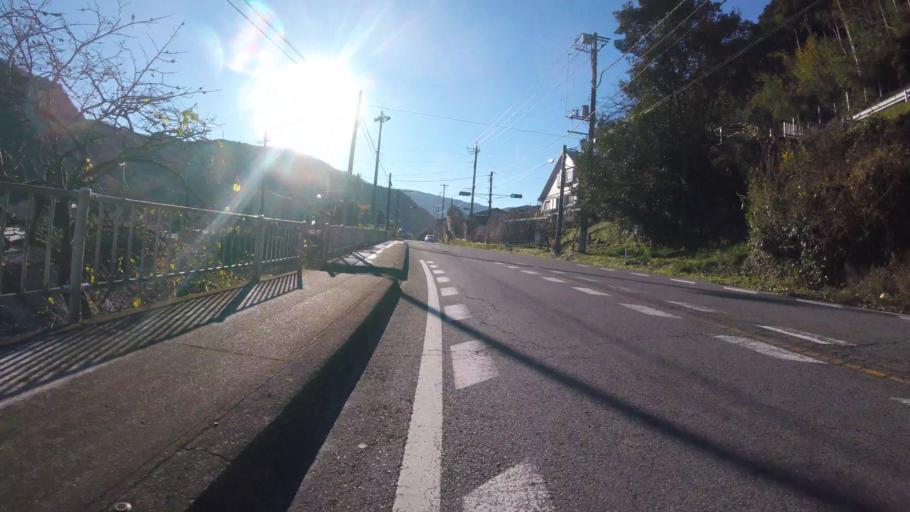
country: JP
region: Shizuoka
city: Heda
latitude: 34.9154
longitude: 138.9234
